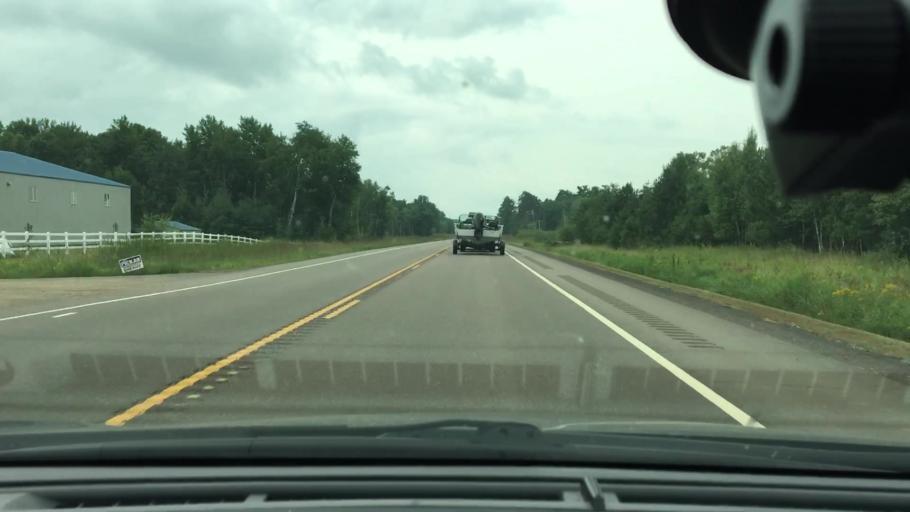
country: US
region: Minnesota
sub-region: Crow Wing County
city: Crosby
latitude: 46.5937
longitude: -93.9527
